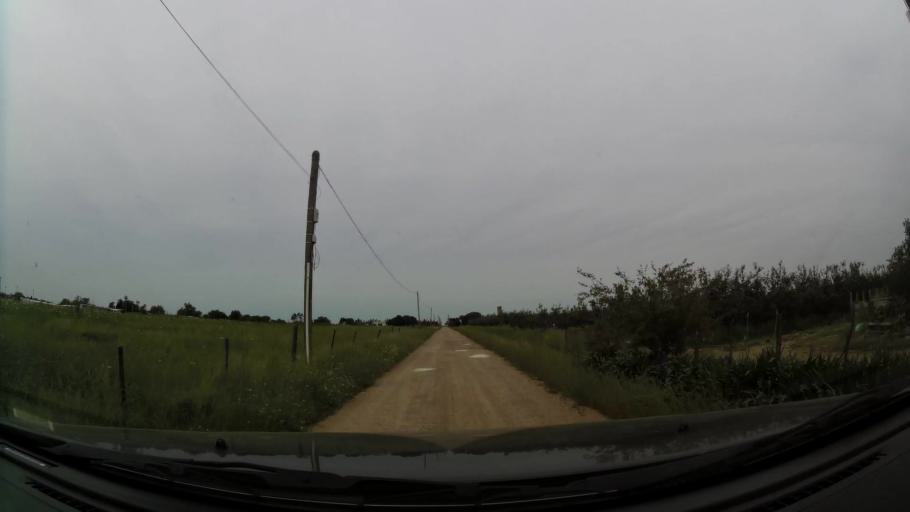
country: UY
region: Canelones
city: Las Piedras
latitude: -34.7412
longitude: -56.2352
